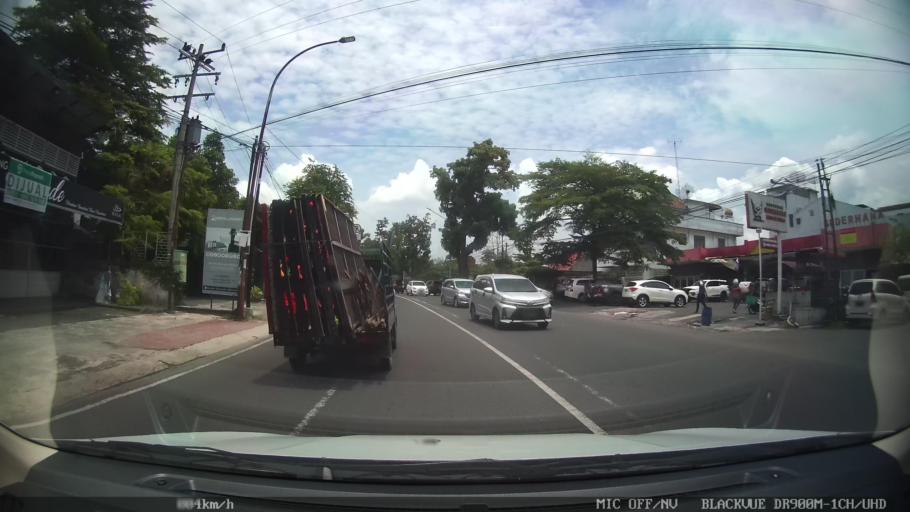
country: ID
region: North Sumatra
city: Medan
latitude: 3.5750
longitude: 98.6655
